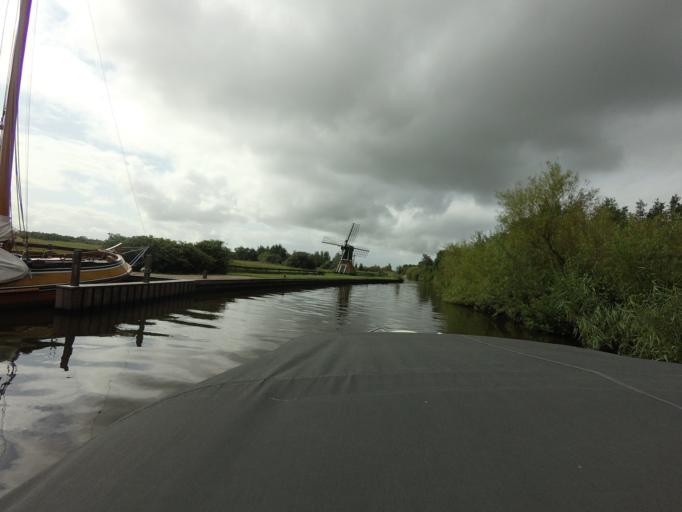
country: NL
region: Friesland
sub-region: Gemeente Boarnsterhim
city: Warten
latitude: 53.1385
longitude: 5.9117
